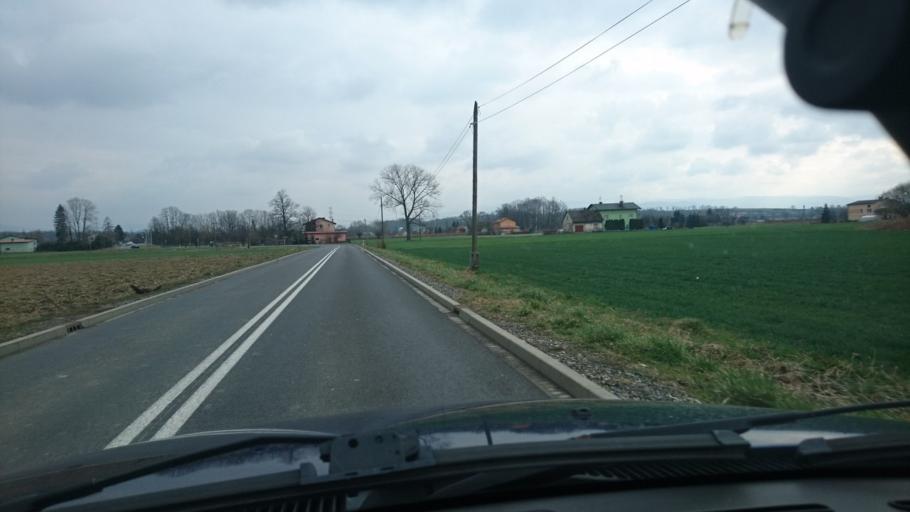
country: PL
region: Silesian Voivodeship
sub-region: Powiat bielski
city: Mazancowice
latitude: 49.8734
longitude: 18.9571
